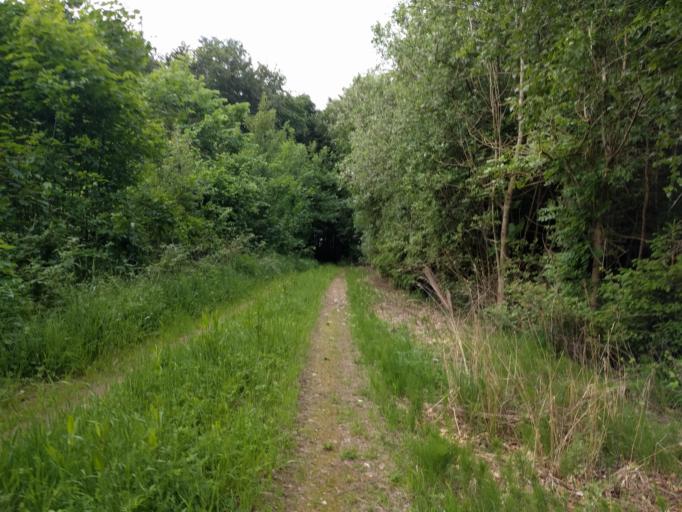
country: DK
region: South Denmark
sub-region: Kerteminde Kommune
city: Kerteminde
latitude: 55.4246
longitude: 10.6104
